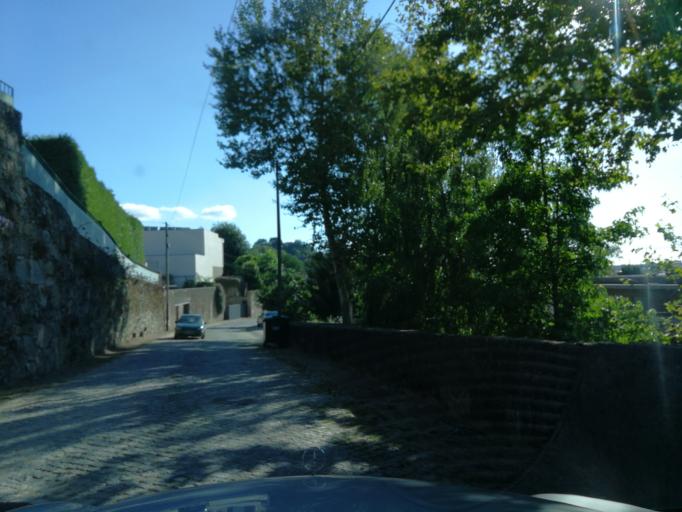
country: PT
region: Braga
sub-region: Braga
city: Adaufe
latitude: 41.5606
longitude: -8.3833
